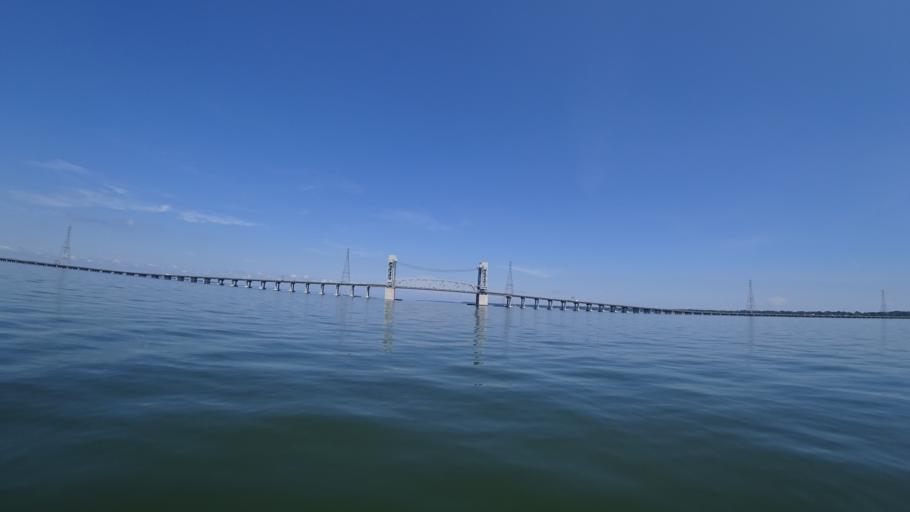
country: US
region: Virginia
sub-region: City of Newport News
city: Newport News
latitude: 36.9991
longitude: -76.4646
